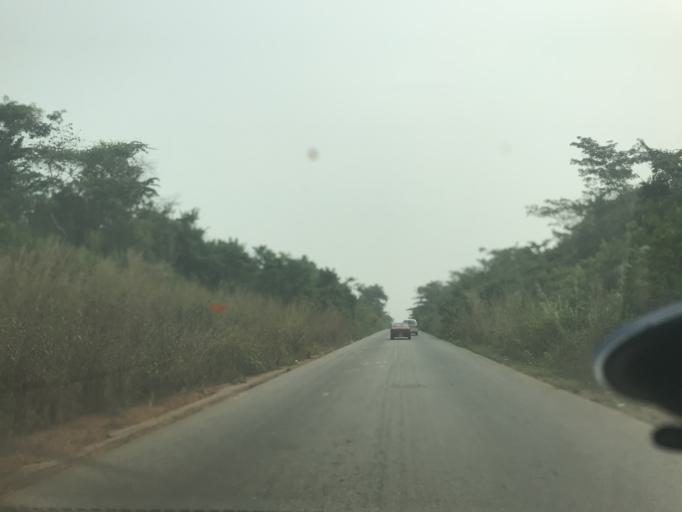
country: NG
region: Ogun
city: Ilaro
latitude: 6.8855
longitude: 3.0717
